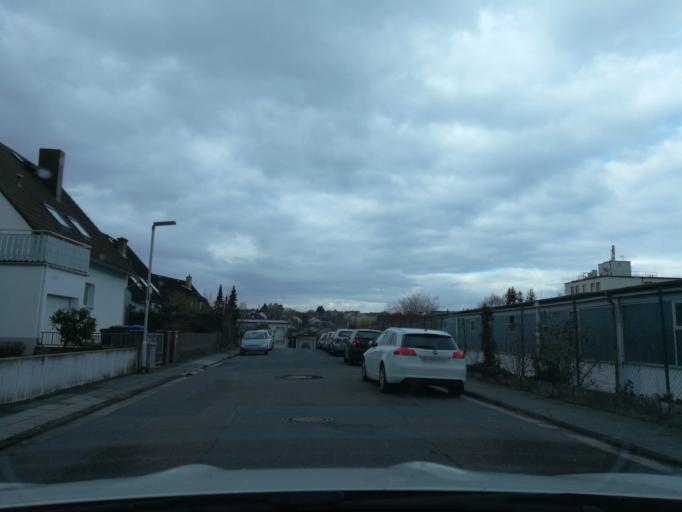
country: DE
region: Hesse
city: Reinheim
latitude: 49.8340
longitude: 8.8355
